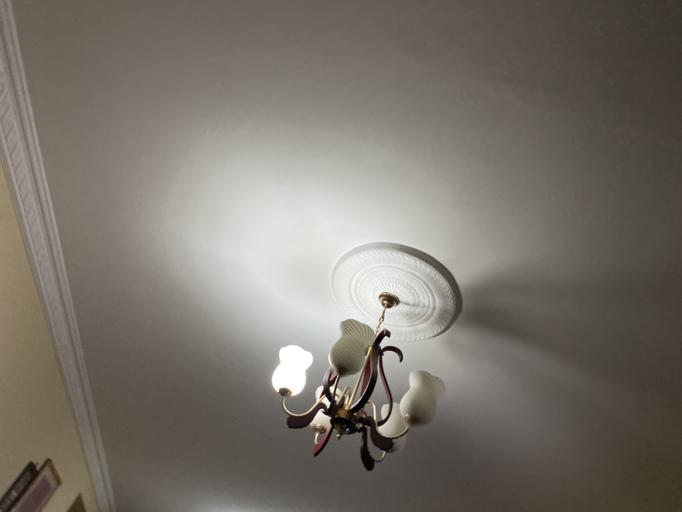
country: ET
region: Adis Abeba
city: Addis Ababa
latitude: 9.0149
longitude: 38.8103
